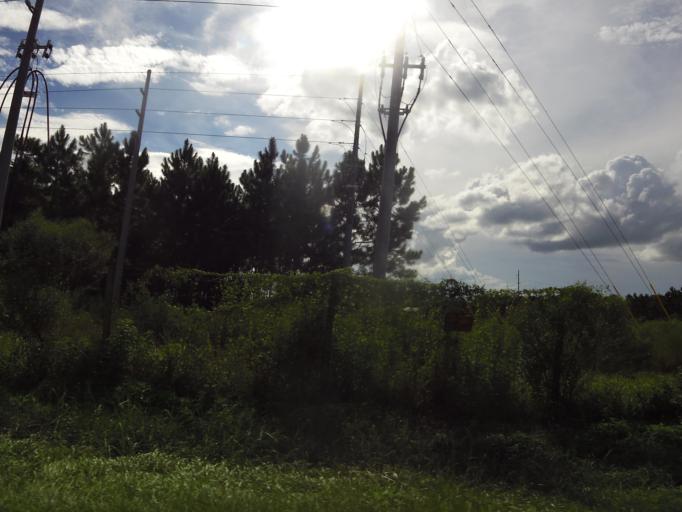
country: US
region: Florida
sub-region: Clay County
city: Green Cove Springs
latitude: 29.9516
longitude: -81.6939
